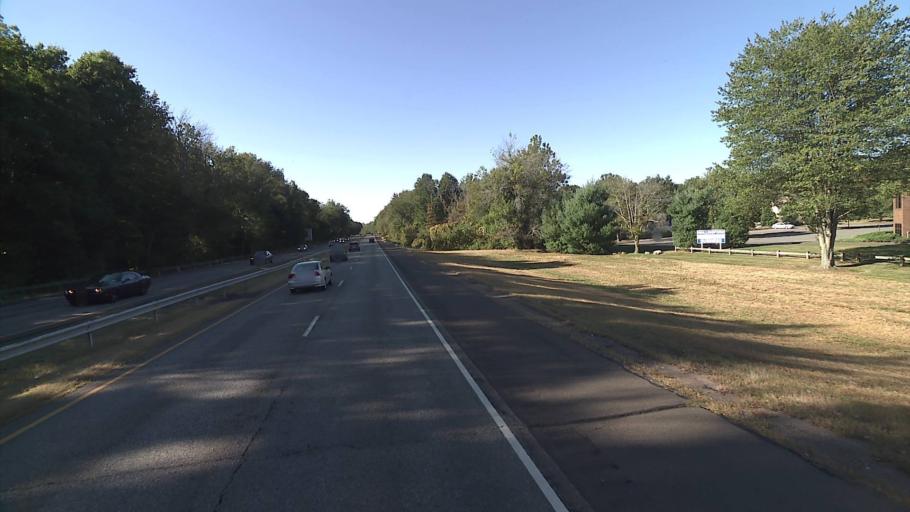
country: US
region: Connecticut
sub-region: New Haven County
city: Wallingford
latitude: 41.4452
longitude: -72.8442
